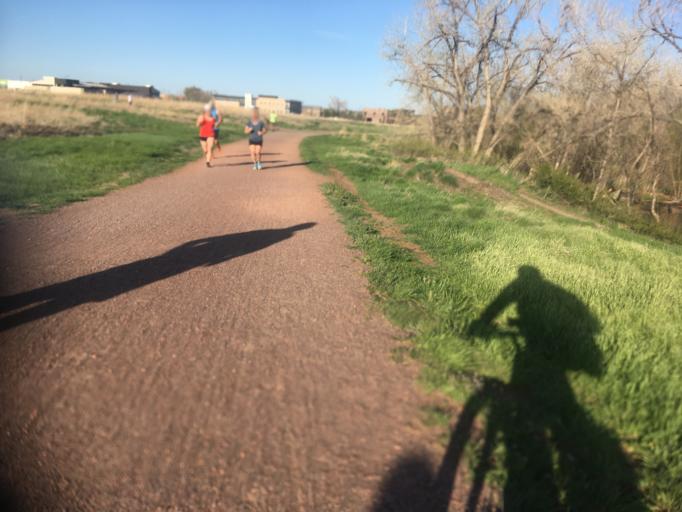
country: US
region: Colorado
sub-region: Boulder County
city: Lafayette
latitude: 39.9806
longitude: -105.0959
